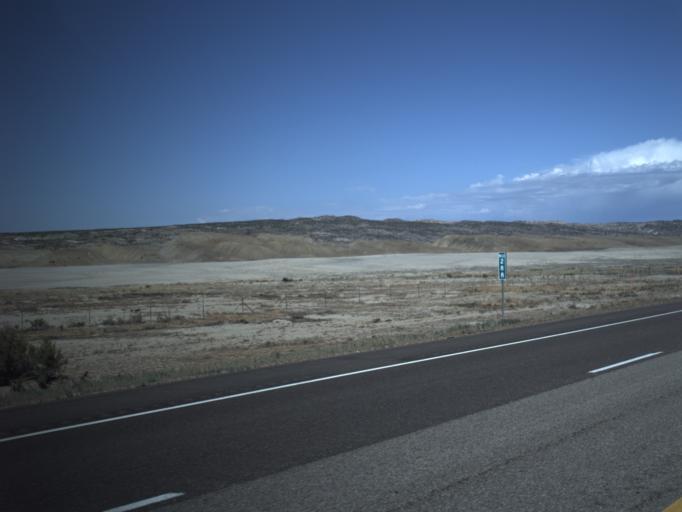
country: US
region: Utah
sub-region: Carbon County
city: East Carbon City
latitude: 39.1262
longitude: -110.3340
